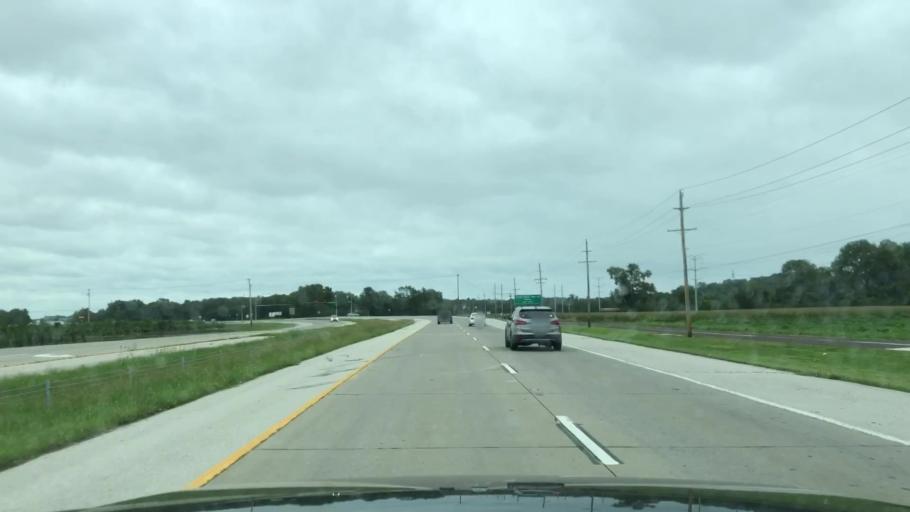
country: US
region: Missouri
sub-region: Saint Charles County
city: Saint Charles
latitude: 38.7304
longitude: -90.4855
